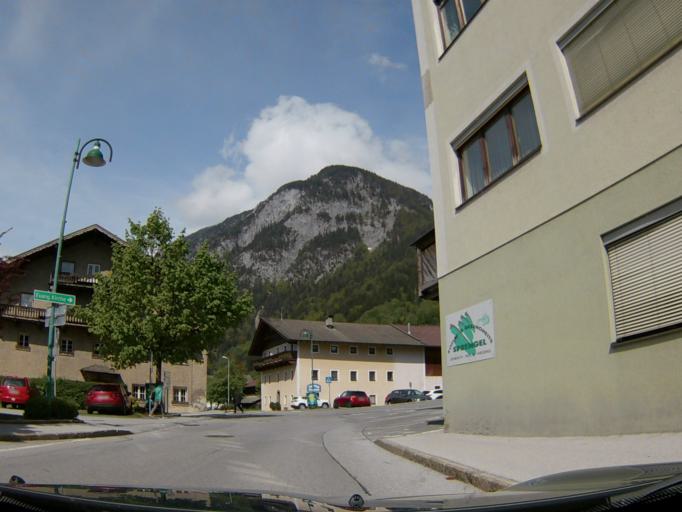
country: AT
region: Tyrol
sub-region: Politischer Bezirk Schwaz
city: Jenbach
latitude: 47.3917
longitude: 11.7709
